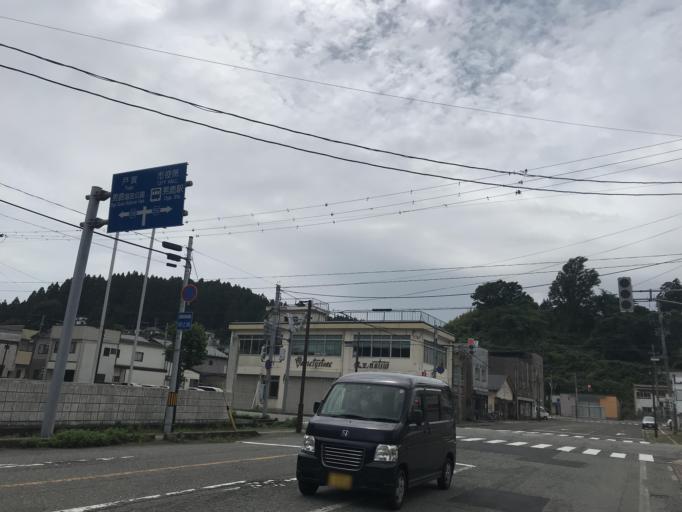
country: JP
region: Akita
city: Tenno
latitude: 39.8828
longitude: 139.8470
